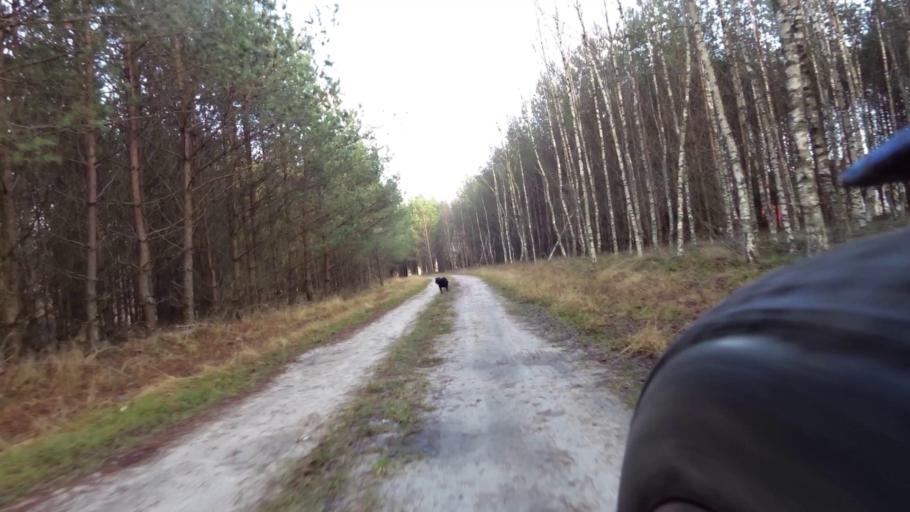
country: PL
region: West Pomeranian Voivodeship
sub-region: Powiat szczecinecki
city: Borne Sulinowo
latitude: 53.6147
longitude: 16.6190
